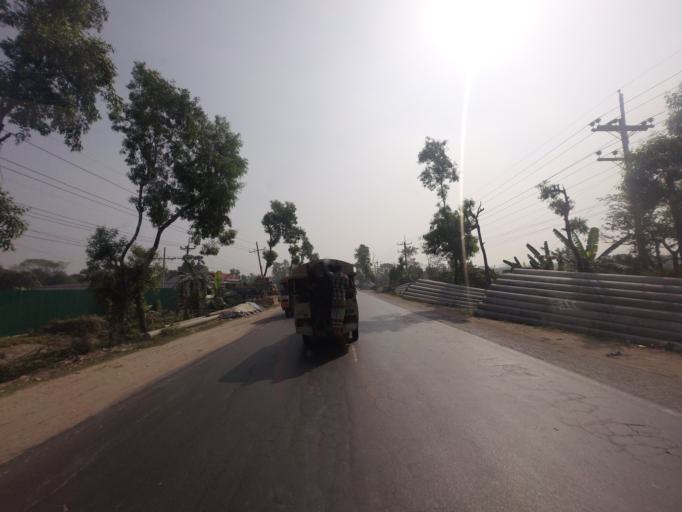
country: BD
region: Dhaka
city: Narsingdi
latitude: 23.8547
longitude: 90.6592
